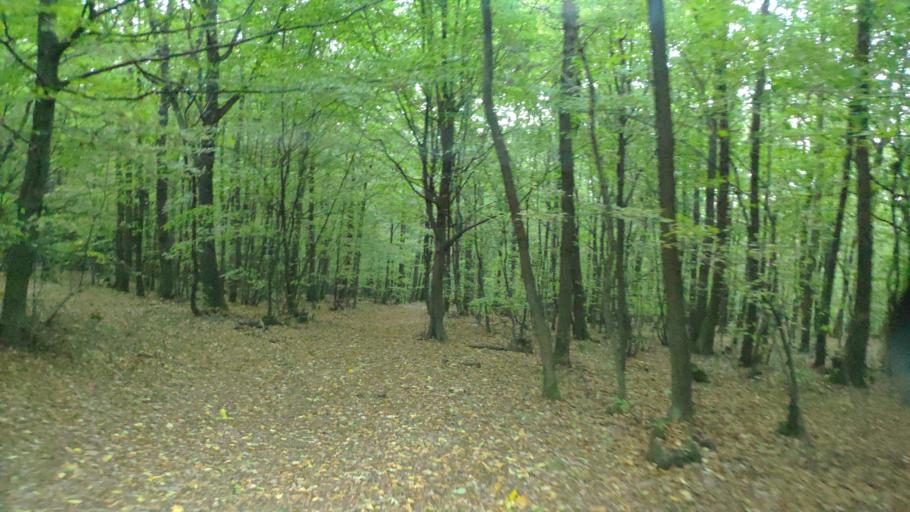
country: SK
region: Kosicky
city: Kosice
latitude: 48.6965
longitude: 21.1969
